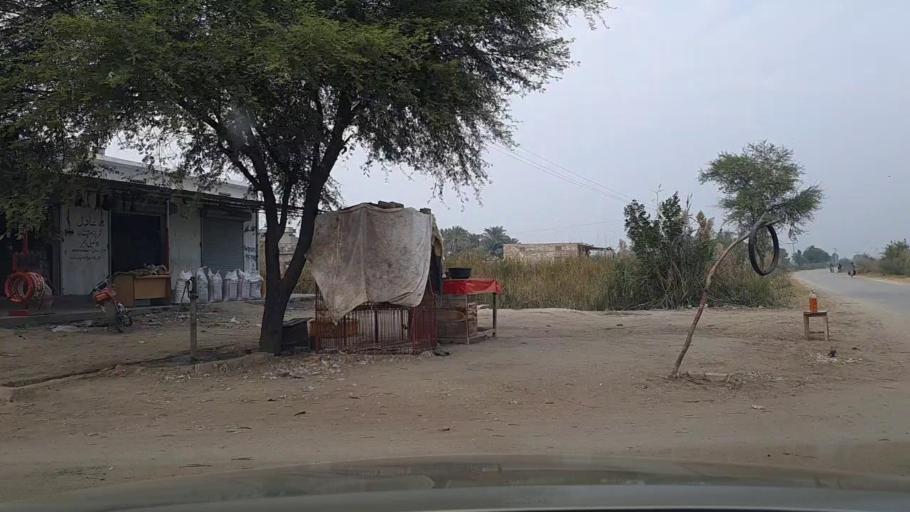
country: PK
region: Sindh
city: Sanghar
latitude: 26.1683
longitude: 68.9591
